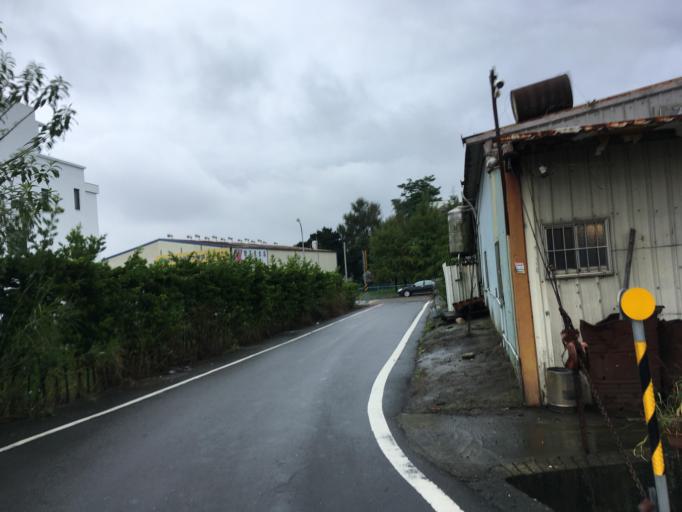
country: TW
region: Taiwan
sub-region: Yilan
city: Yilan
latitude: 24.6651
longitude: 121.7492
